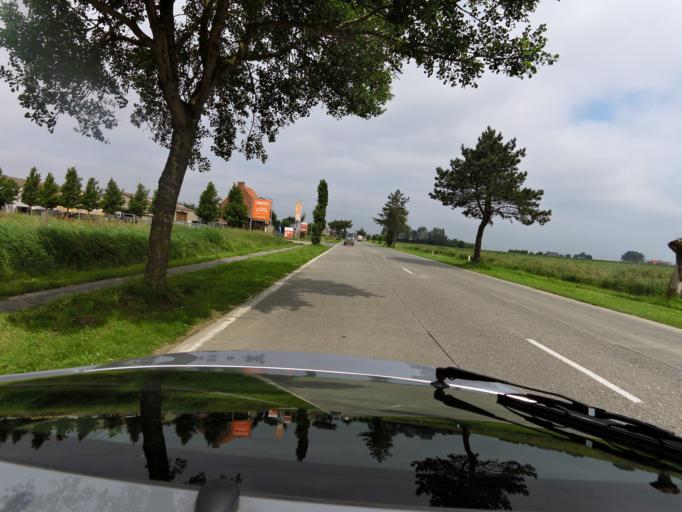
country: BE
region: Flanders
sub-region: Provincie West-Vlaanderen
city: Alveringem
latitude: 50.9549
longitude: 2.7162
